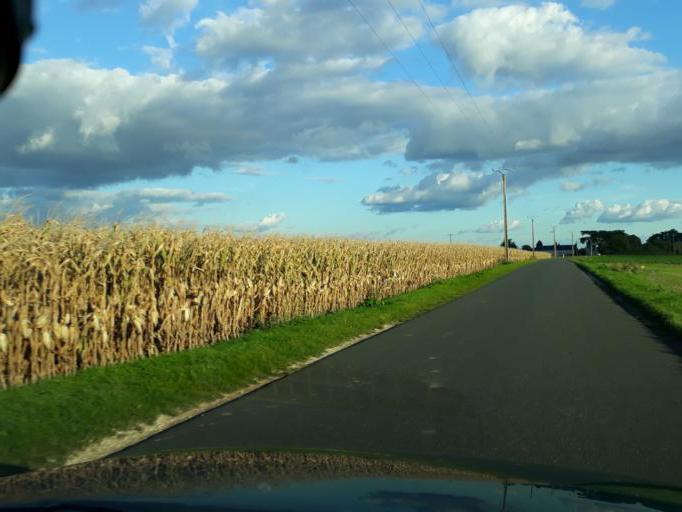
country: FR
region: Centre
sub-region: Departement du Loiret
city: Tavers
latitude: 47.7815
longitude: 1.5384
